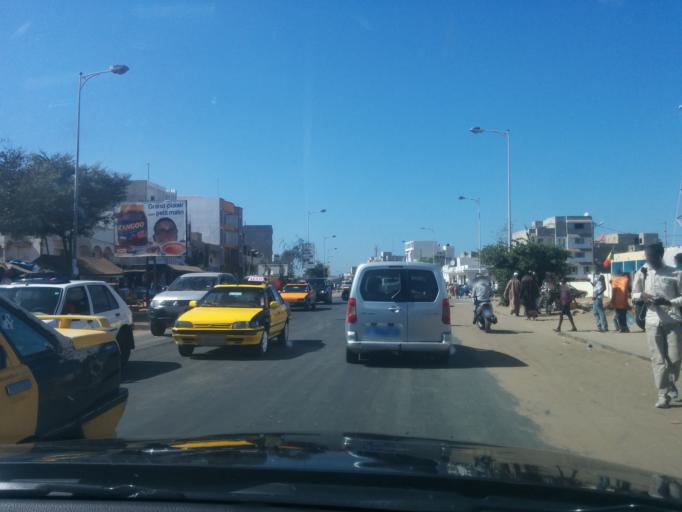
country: SN
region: Dakar
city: Grand Dakar
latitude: 14.7506
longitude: -17.4405
